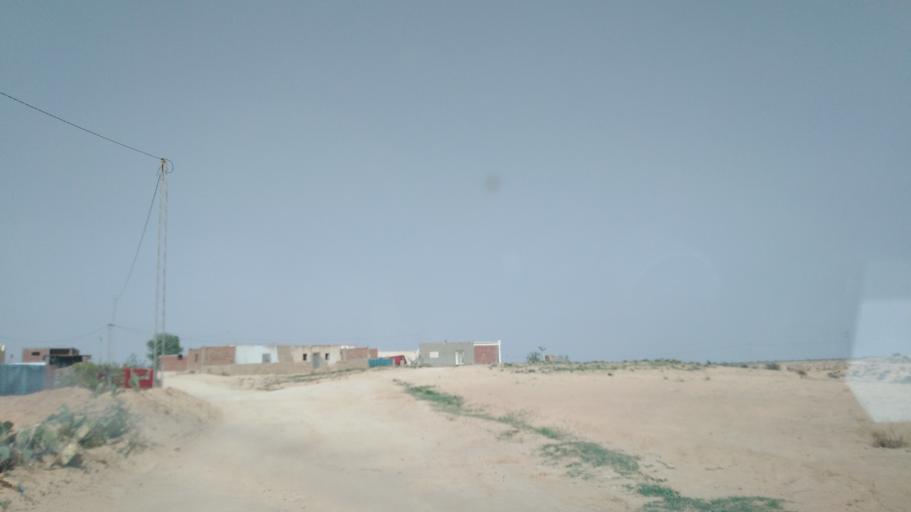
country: TN
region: Safaqis
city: Sfax
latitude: 34.6412
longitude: 10.5622
